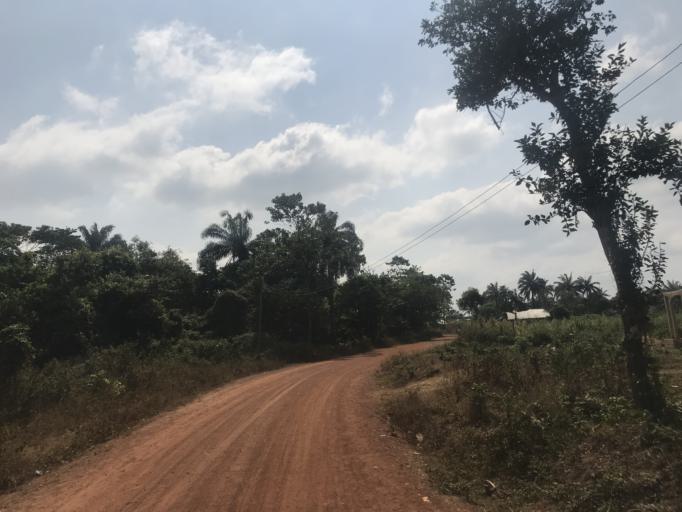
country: NG
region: Osun
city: Ibokun
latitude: 7.8028
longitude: 4.6522
